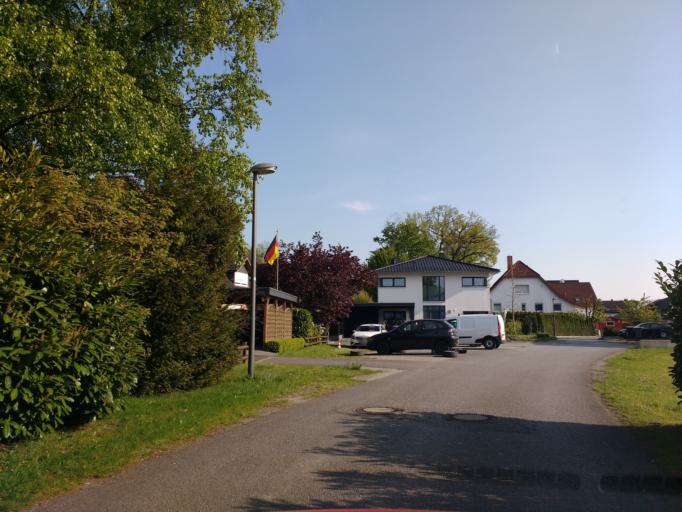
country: DE
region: North Rhine-Westphalia
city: Bad Lippspringe
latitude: 51.7659
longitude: 8.7815
